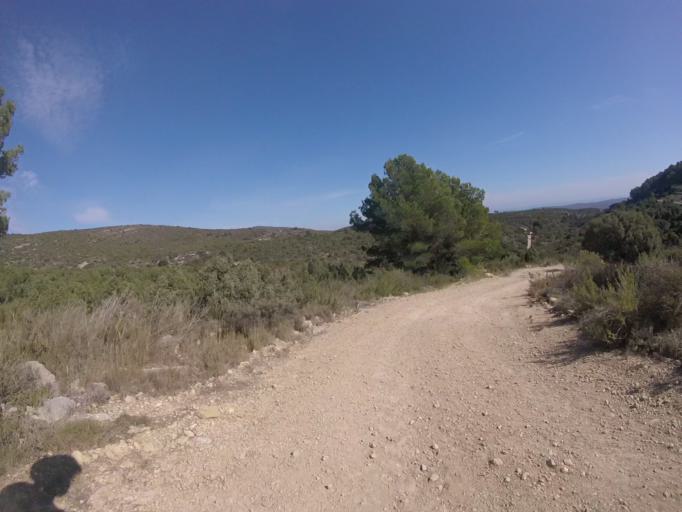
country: ES
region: Valencia
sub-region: Provincia de Castello
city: Sierra-Engarceran
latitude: 40.2708
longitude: 0.0112
